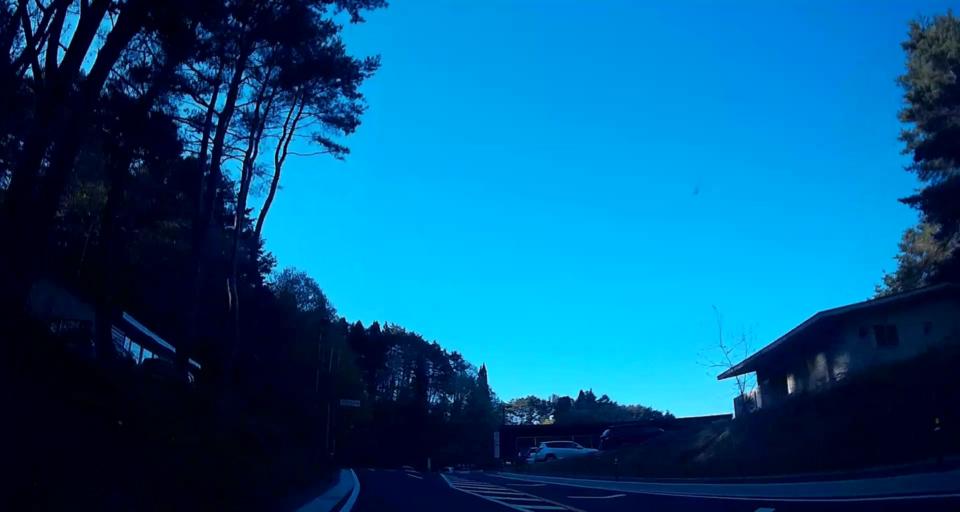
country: JP
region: Iwate
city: Miyako
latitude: 39.6456
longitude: 141.9777
